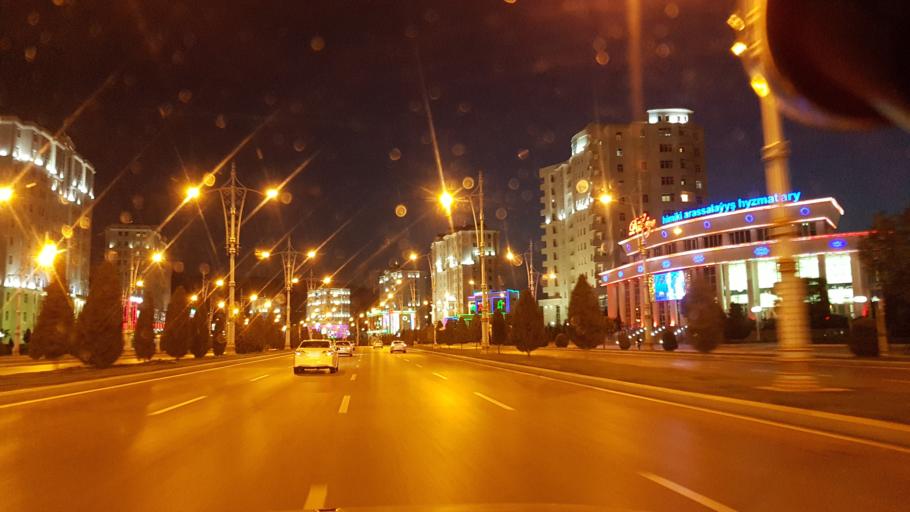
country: TM
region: Ahal
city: Ashgabat
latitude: 37.9185
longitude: 58.3509
